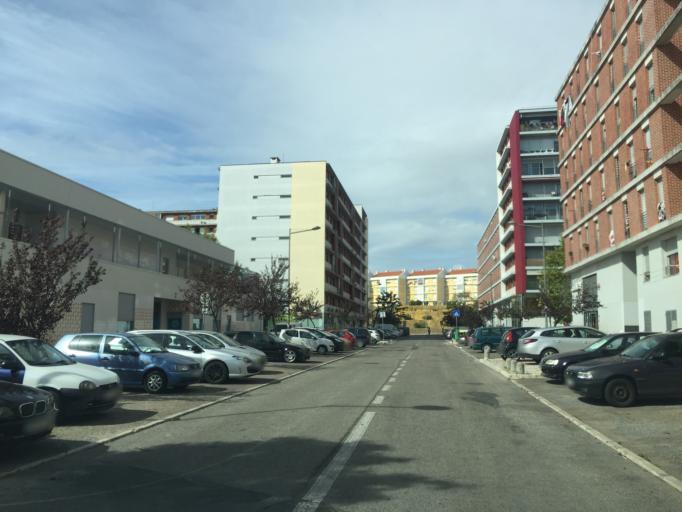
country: PT
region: Lisbon
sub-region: Odivelas
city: Olival do Basto
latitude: 38.7748
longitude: -9.1506
